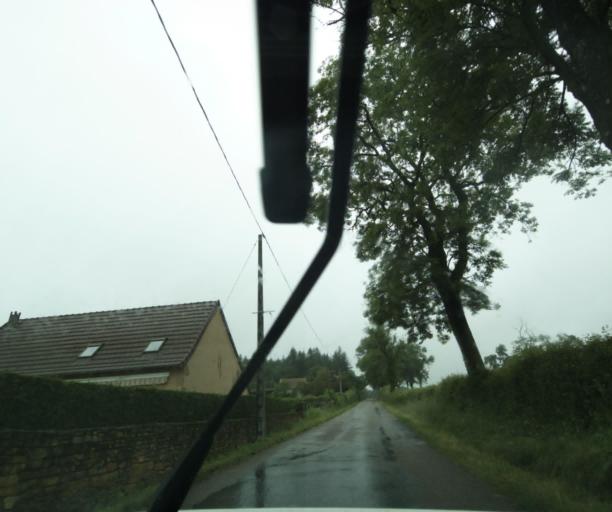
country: FR
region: Bourgogne
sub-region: Departement de Saone-et-Loire
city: Charolles
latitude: 46.4151
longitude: 4.1988
